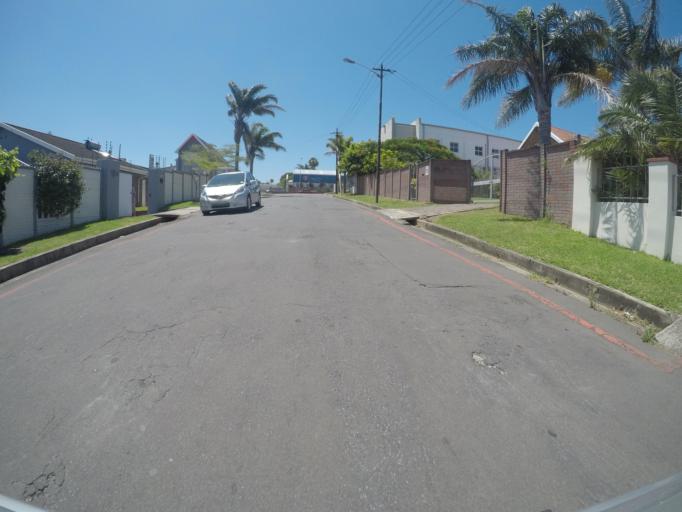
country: ZA
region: Eastern Cape
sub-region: Buffalo City Metropolitan Municipality
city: East London
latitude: -32.9853
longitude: 27.9075
